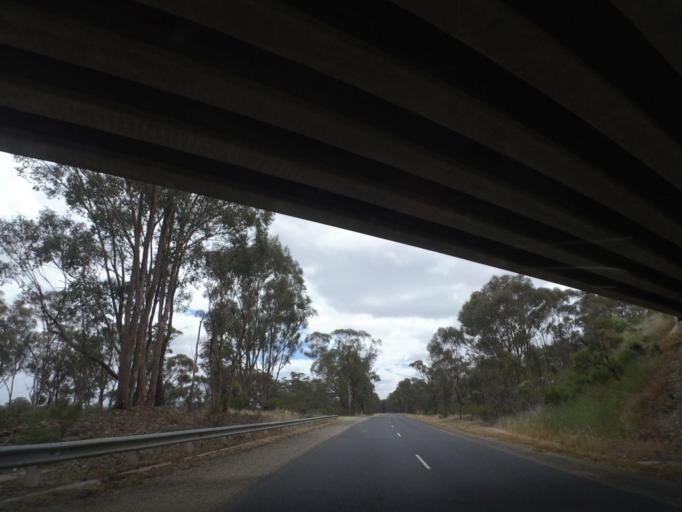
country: AU
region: Victoria
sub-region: Murrindindi
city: Kinglake West
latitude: -36.9831
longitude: 145.1604
